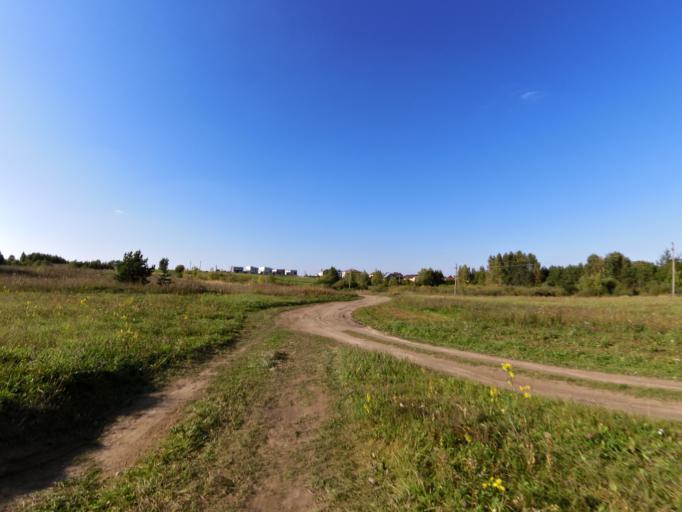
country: LT
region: Vilnius County
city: Pilaite
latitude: 54.7205
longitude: 25.1815
